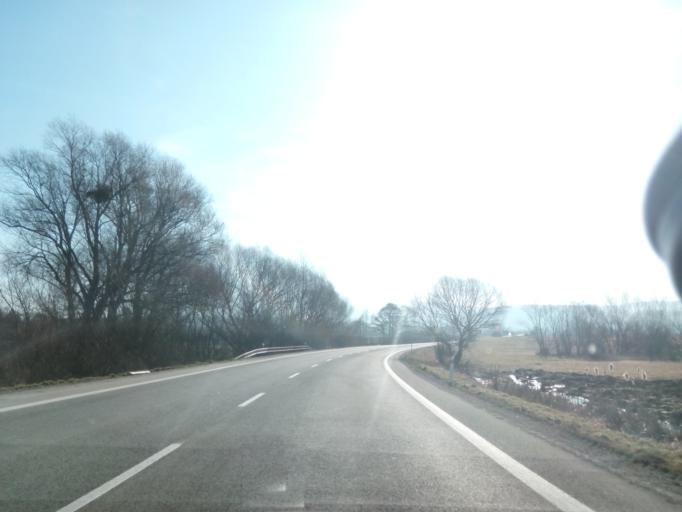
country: SK
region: Kosicky
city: Kosice
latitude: 48.7361
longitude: 21.4307
